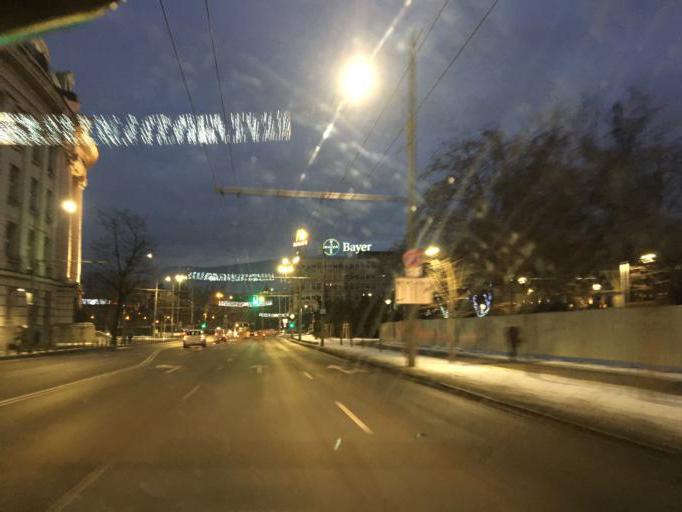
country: BG
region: Sofia-Capital
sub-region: Stolichna Obshtina
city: Sofia
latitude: 42.6945
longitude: 23.3346
